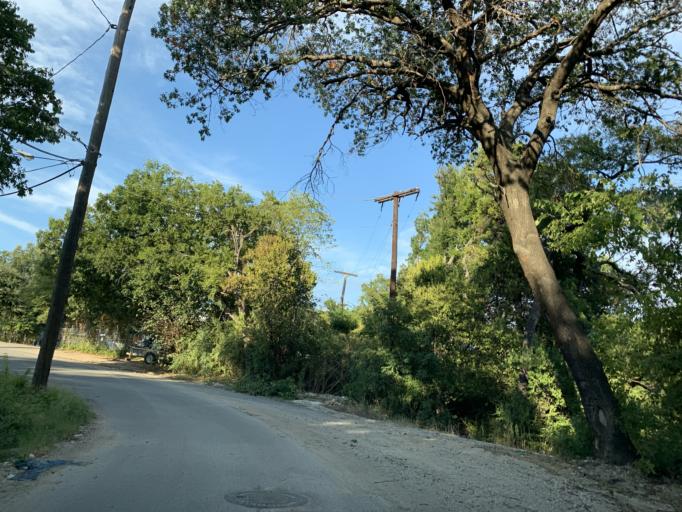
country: US
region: Texas
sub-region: Dallas County
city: Dallas
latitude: 32.7383
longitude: -96.8179
